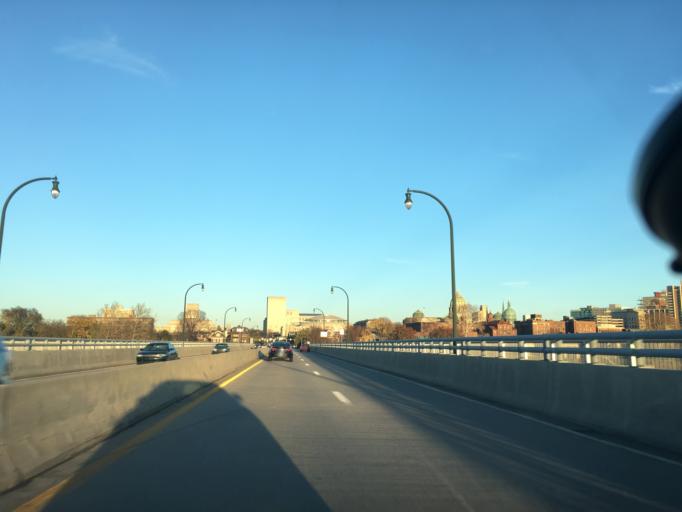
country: US
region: Pennsylvania
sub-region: Dauphin County
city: Harrisburg
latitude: 40.2637
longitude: -76.8941
